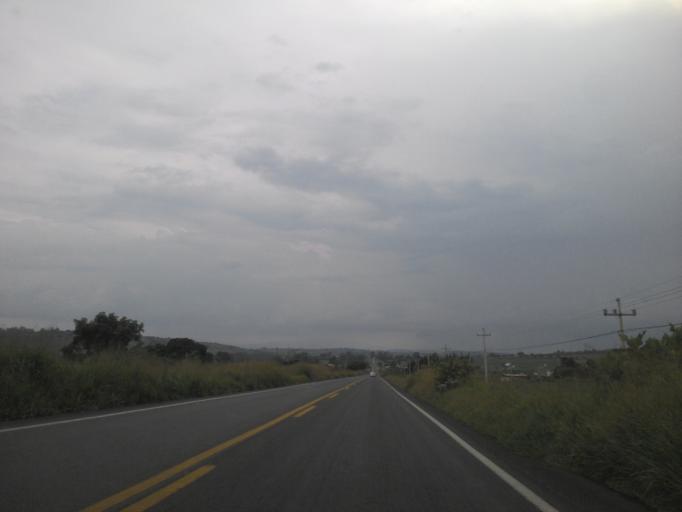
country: MX
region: Jalisco
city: Zapotlanejo
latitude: 20.6932
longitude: -102.9826
